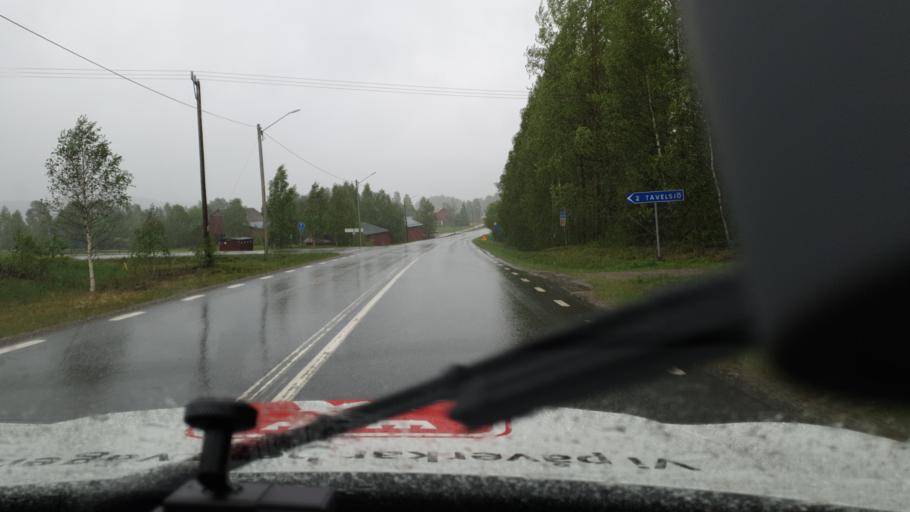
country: SE
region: Vaesterbotten
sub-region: Vannas Kommun
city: Vannasby
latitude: 64.0275
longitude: 20.0210
